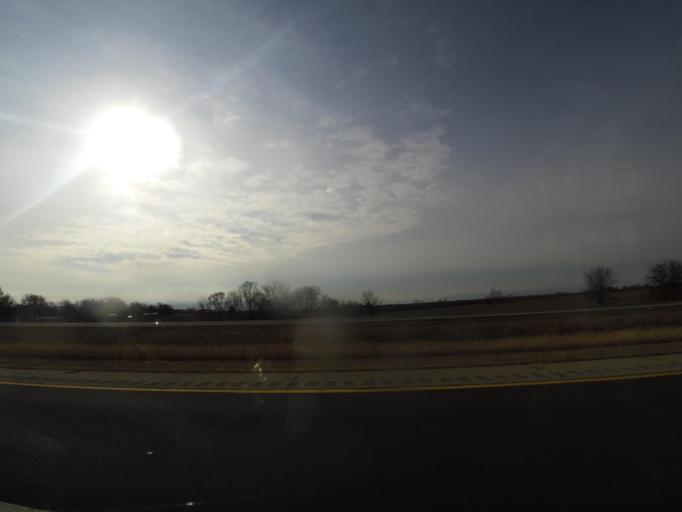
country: US
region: Illinois
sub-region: Macon County
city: Decatur
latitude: 39.7868
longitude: -88.9828
